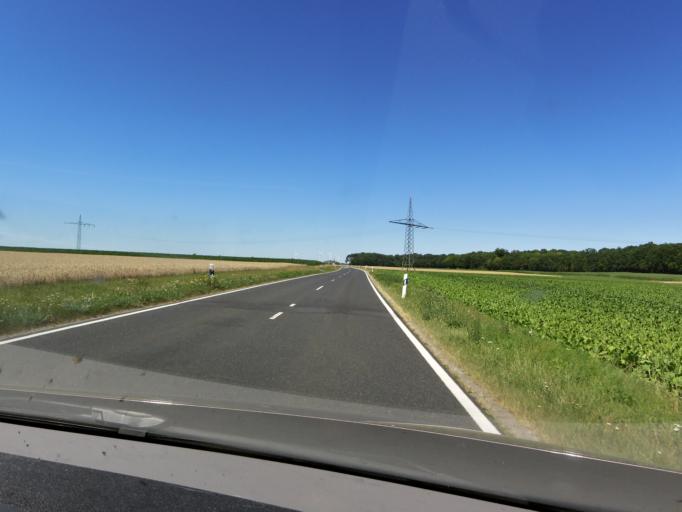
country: DE
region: Bavaria
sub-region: Regierungsbezirk Unterfranken
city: Frickenhausen
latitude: 49.7144
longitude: 10.0808
